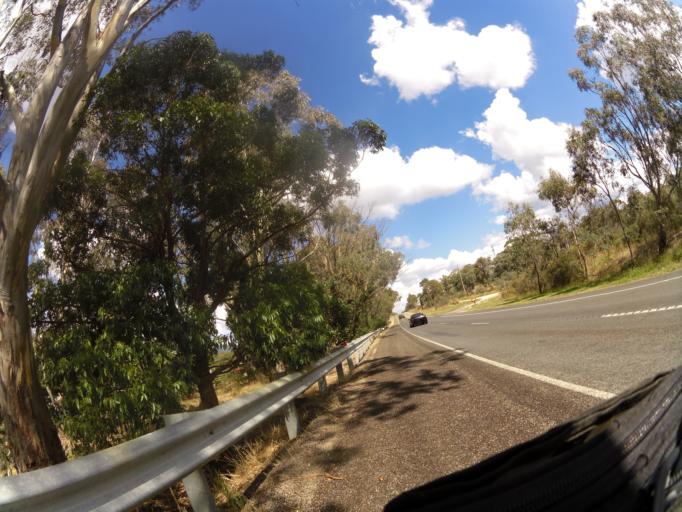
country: AU
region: Victoria
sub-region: Benalla
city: Benalla
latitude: -36.7890
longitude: 146.0107
